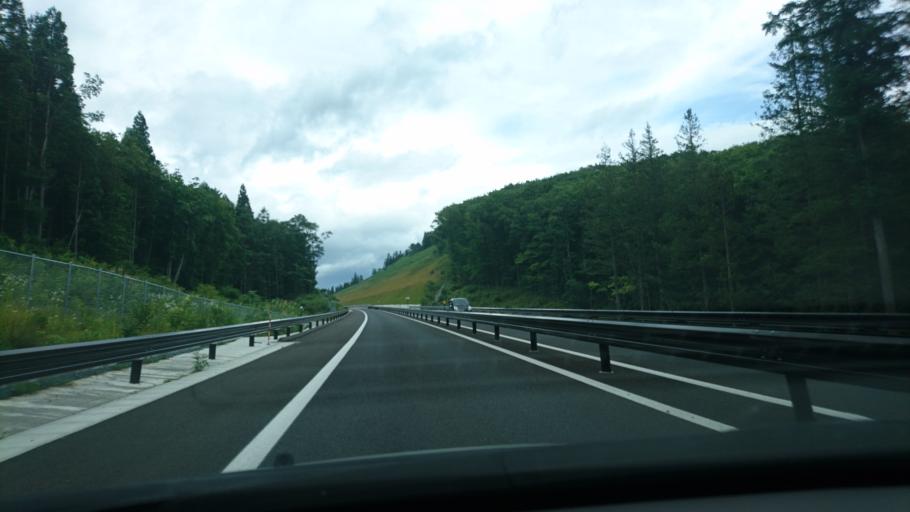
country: JP
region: Iwate
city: Yamada
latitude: 39.5474
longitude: 141.9250
